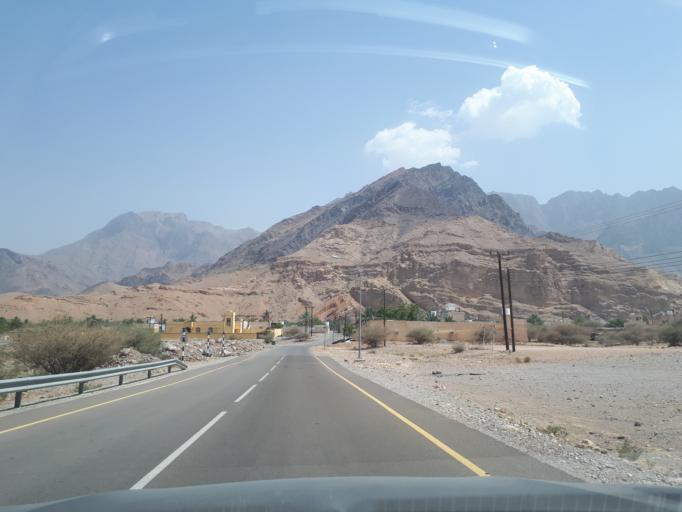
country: OM
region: Ash Sharqiyah
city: Ibra'
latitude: 23.0892
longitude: 58.8520
